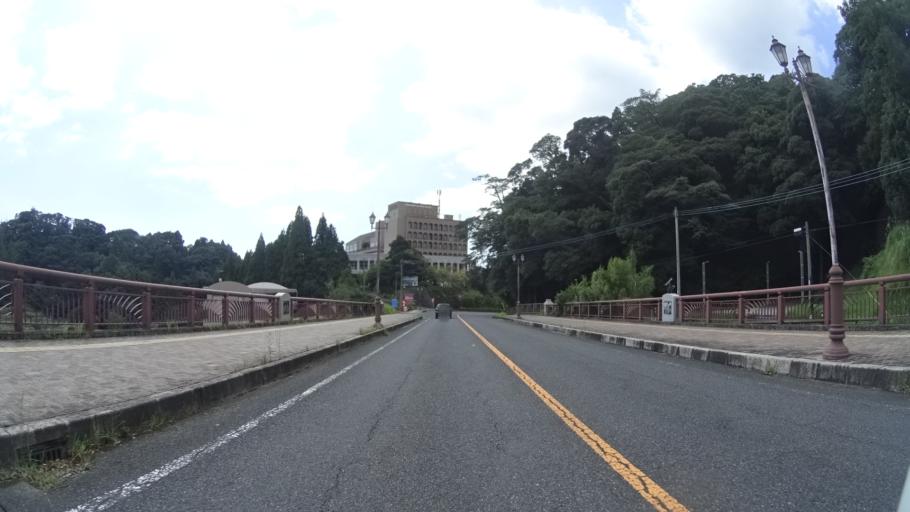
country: JP
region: Kagoshima
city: Kokubu-matsuki
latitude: 31.8916
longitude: 130.8258
